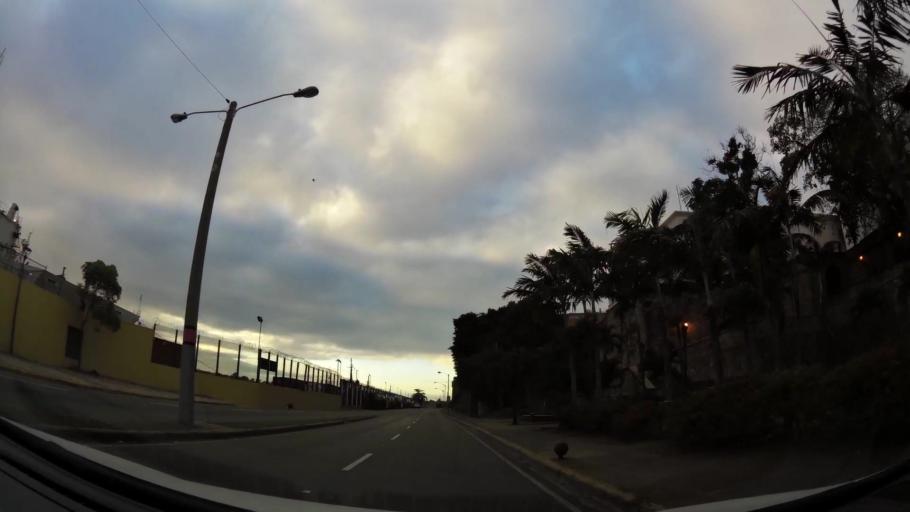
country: DO
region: Nacional
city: Ciudad Nueva
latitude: 18.4747
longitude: -69.8820
